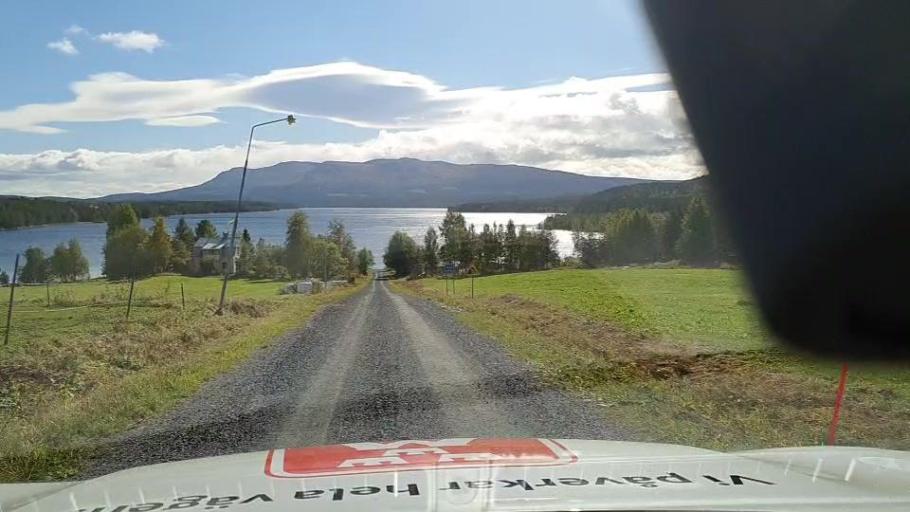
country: SE
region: Jaemtland
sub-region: Are Kommun
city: Jarpen
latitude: 63.2316
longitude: 13.6838
